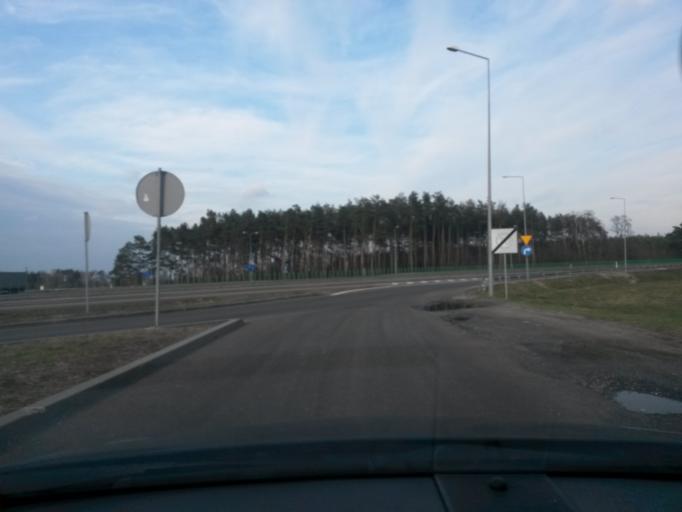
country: PL
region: Lodz Voivodeship
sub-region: Powiat zgierski
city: Zgierz
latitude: 51.9185
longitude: 19.4087
